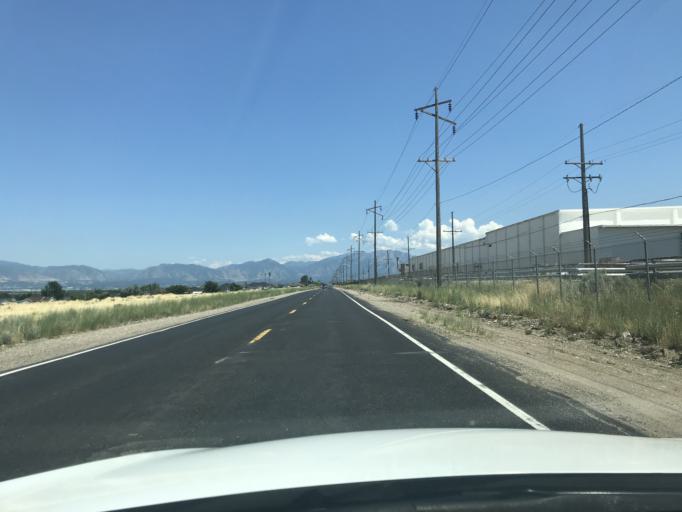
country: US
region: Utah
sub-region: Salt Lake County
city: Magna
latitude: 40.6820
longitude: -112.0674
